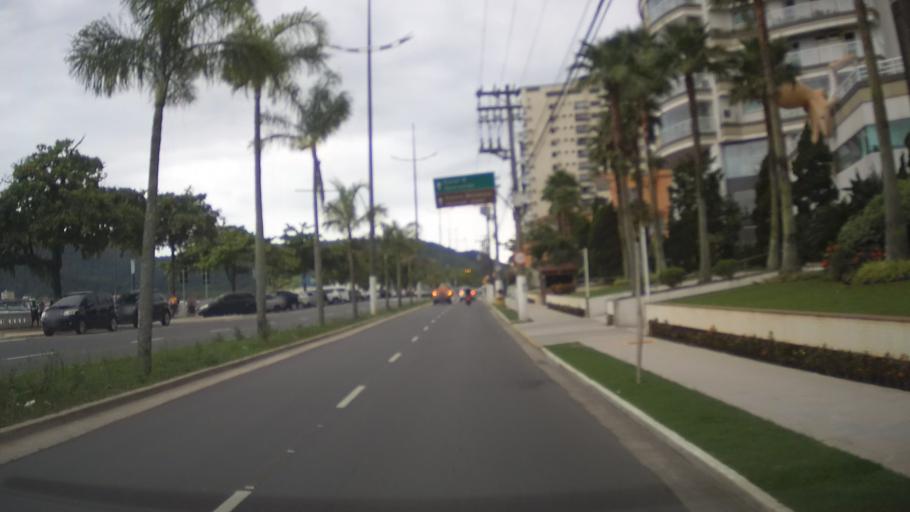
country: BR
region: Sao Paulo
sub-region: Guaruja
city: Guaruja
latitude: -23.9901
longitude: -46.2999
